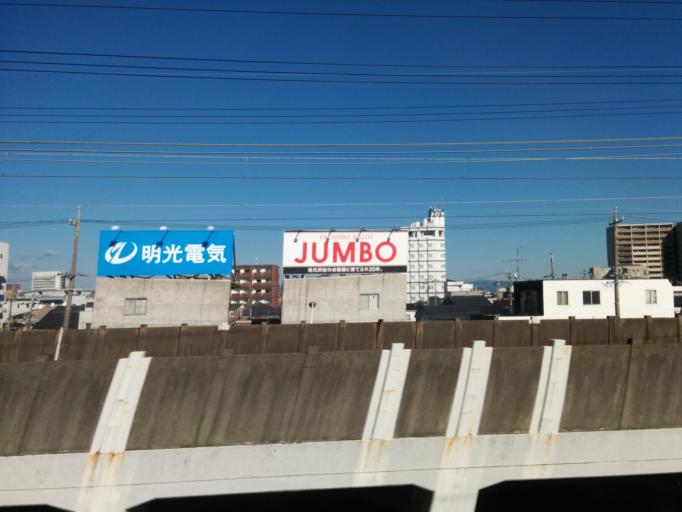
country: JP
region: Shizuoka
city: Hamamatsu
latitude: 34.7067
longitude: 137.7445
